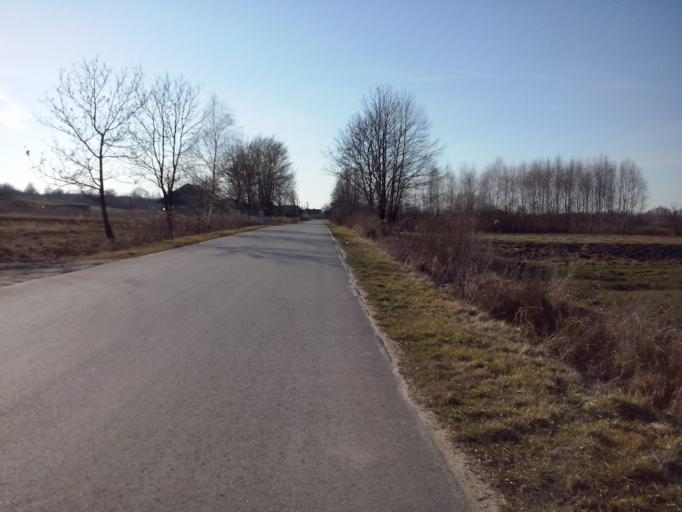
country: PL
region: Subcarpathian Voivodeship
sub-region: Powiat nizanski
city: Krzeszow
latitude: 50.4107
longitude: 22.3615
